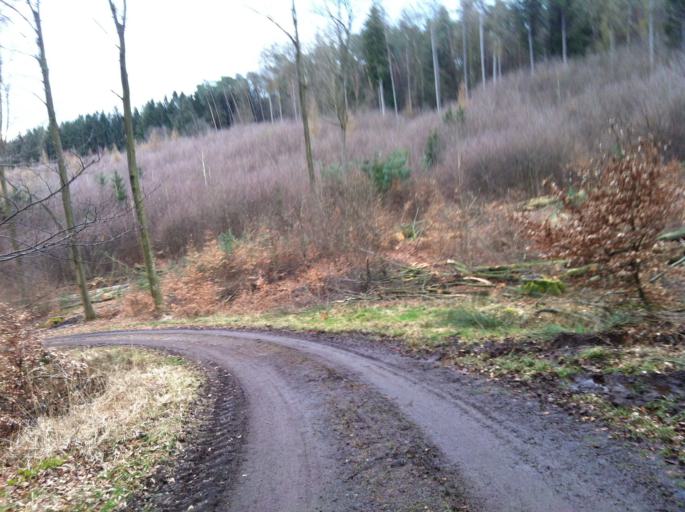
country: DE
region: Hesse
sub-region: Regierungsbezirk Darmstadt
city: Erbach
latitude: 49.6730
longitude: 8.9523
